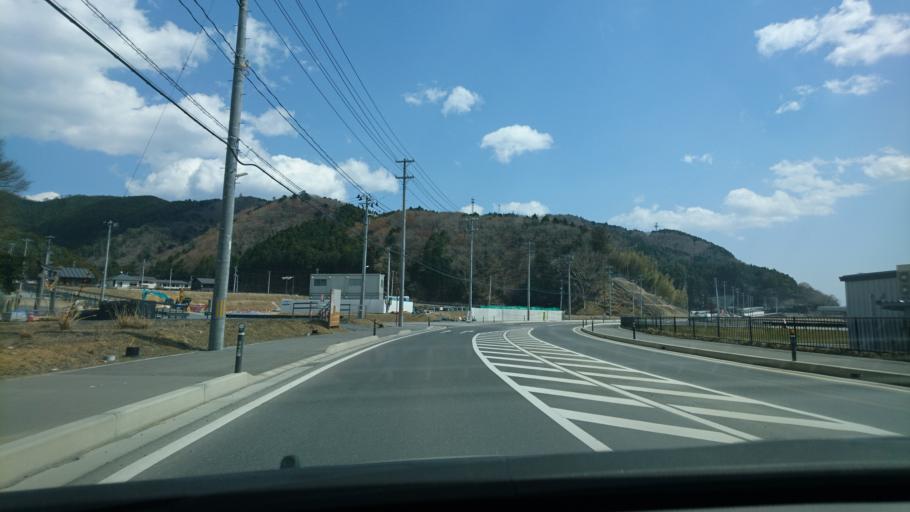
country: JP
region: Miyagi
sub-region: Oshika Gun
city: Onagawa Cho
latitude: 38.4477
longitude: 141.4595
